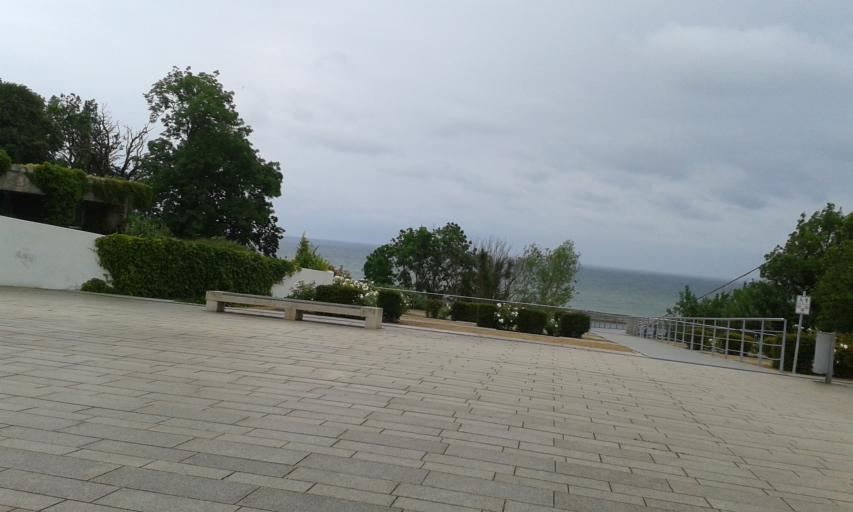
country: DE
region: Mecklenburg-Vorpommern
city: Sassnitz
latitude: 54.5142
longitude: 13.6414
